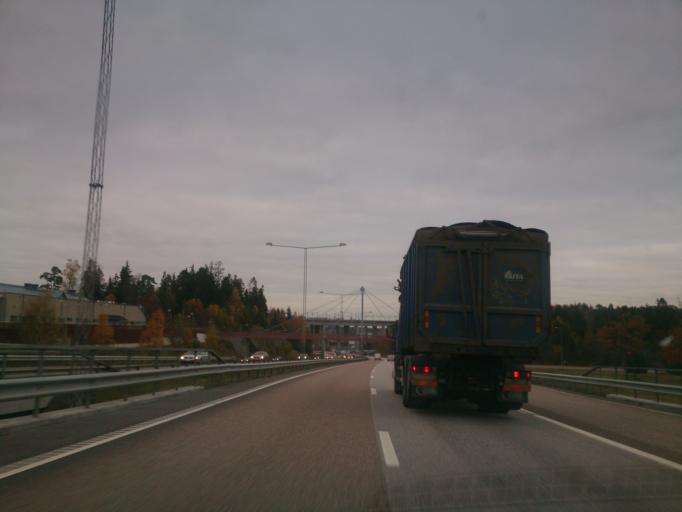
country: SE
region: Stockholm
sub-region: Sodertalje Kommun
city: Pershagen
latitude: 59.1581
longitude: 17.6461
